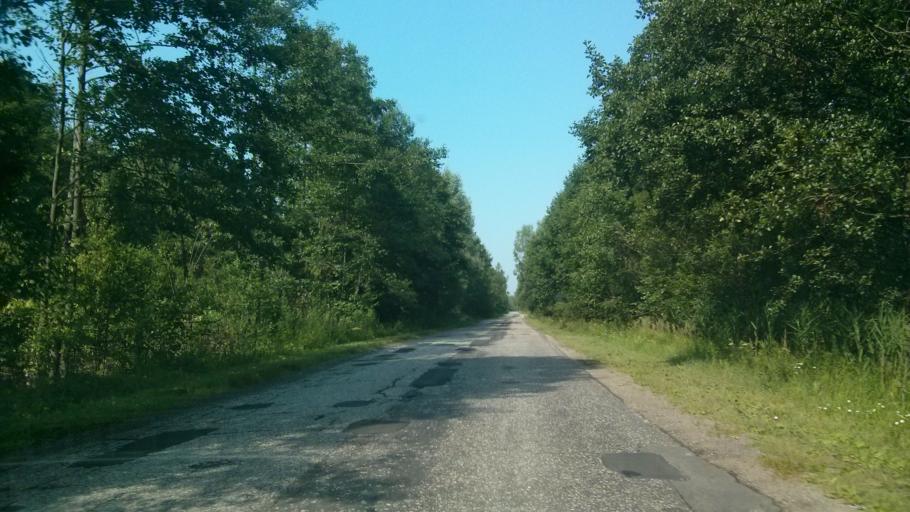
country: RU
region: Vladimir
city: Murom
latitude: 55.5051
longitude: 42.0122
